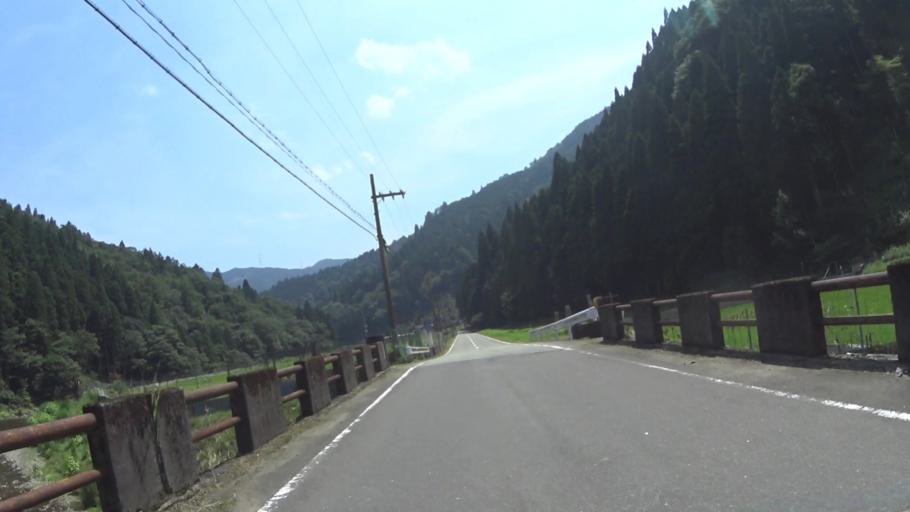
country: JP
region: Kyoto
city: Maizuru
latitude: 35.3399
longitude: 135.5339
